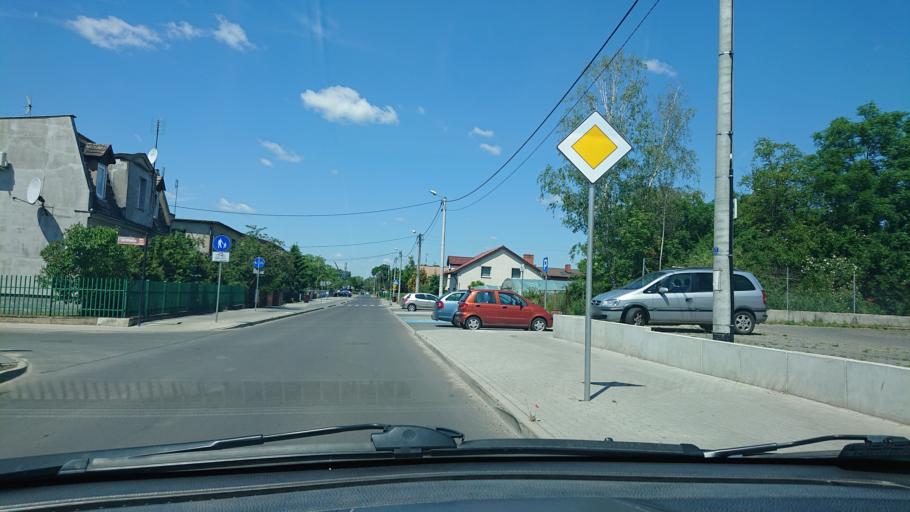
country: PL
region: Greater Poland Voivodeship
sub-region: Powiat gnieznienski
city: Gniezno
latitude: 52.5217
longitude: 17.6124
